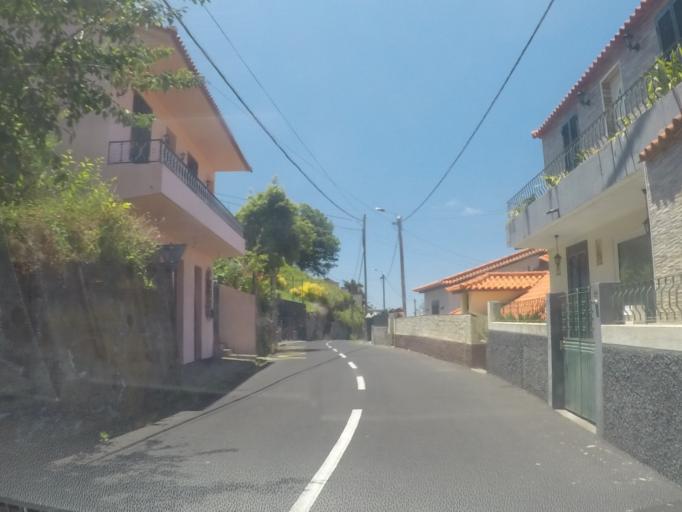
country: PT
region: Madeira
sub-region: Camara de Lobos
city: Curral das Freiras
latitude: 32.6862
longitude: -16.9930
